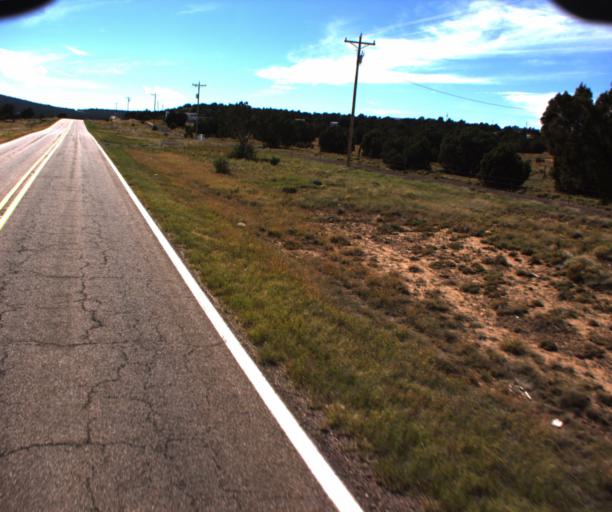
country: US
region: Arizona
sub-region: Navajo County
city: White Mountain Lake
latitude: 34.3331
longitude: -109.7429
